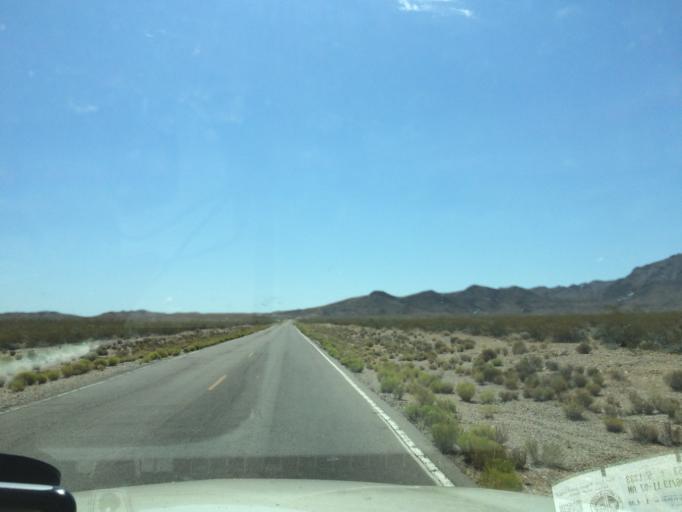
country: US
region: Nevada
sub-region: Clark County
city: Moapa Town
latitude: 36.4496
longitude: -114.6860
